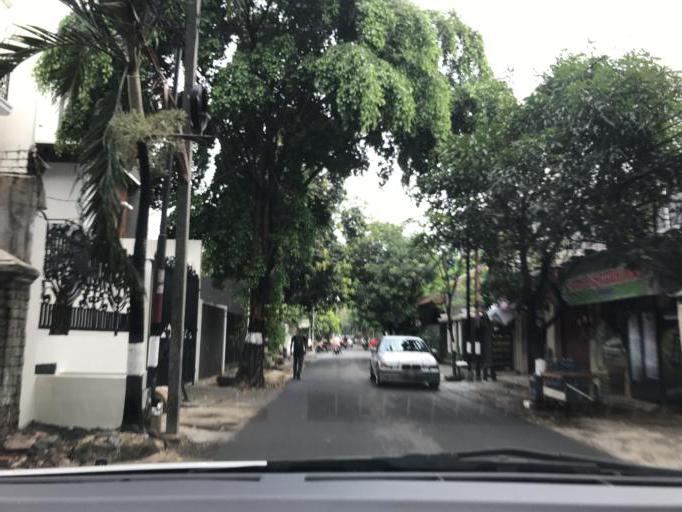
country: ID
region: Jakarta Raya
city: Jakarta
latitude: -6.2874
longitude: 106.8048
